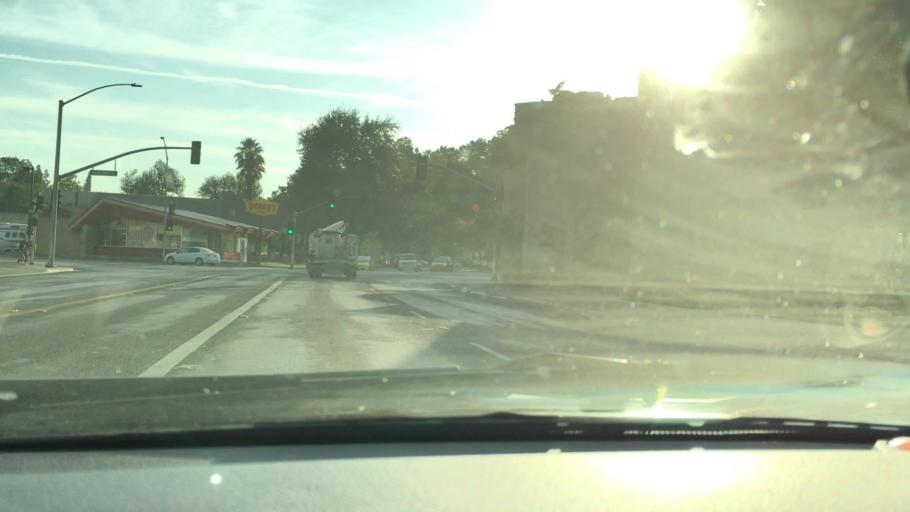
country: US
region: California
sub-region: Stanislaus County
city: Modesto
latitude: 37.6456
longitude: -120.9945
